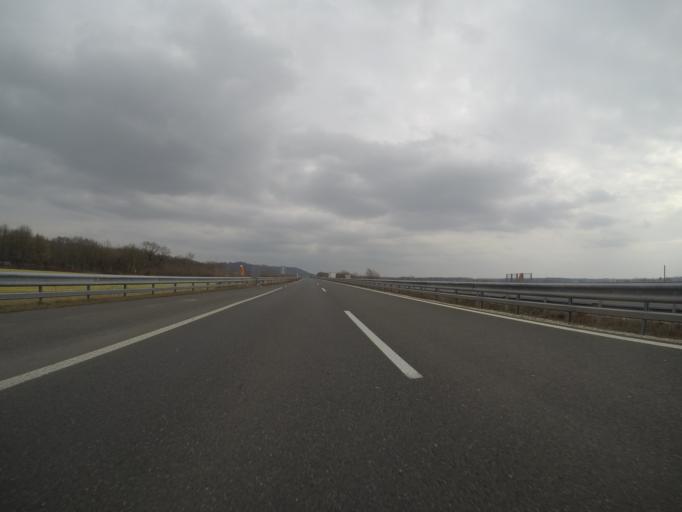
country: HR
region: Medimurska
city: Peklenica
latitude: 46.5283
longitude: 16.4955
